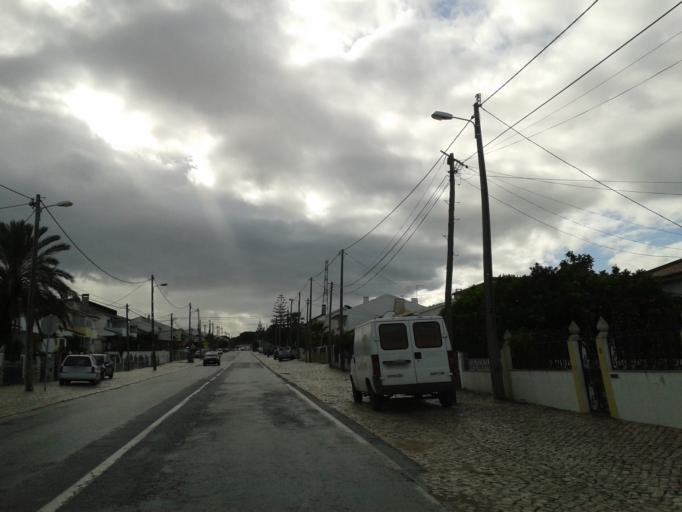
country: PT
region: Setubal
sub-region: Palmela
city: Palmela
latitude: 38.5821
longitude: -8.8902
